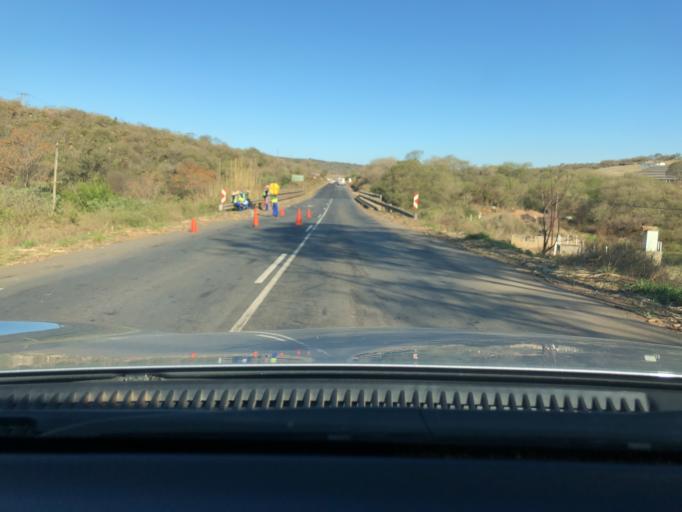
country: ZA
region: KwaZulu-Natal
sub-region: uMgungundlovu District Municipality
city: Camperdown
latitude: -29.8031
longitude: 30.5160
